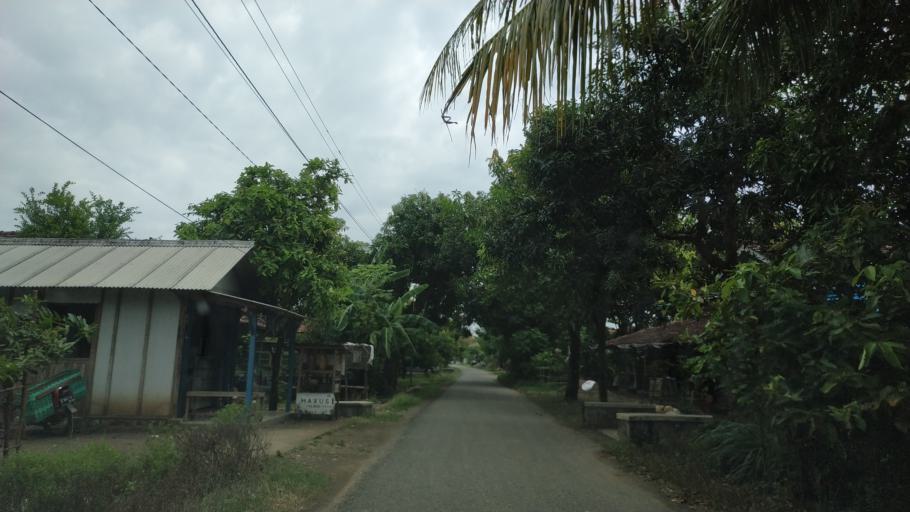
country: ID
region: Central Java
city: Krajan Tegalombo
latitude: -6.4222
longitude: 110.9808
